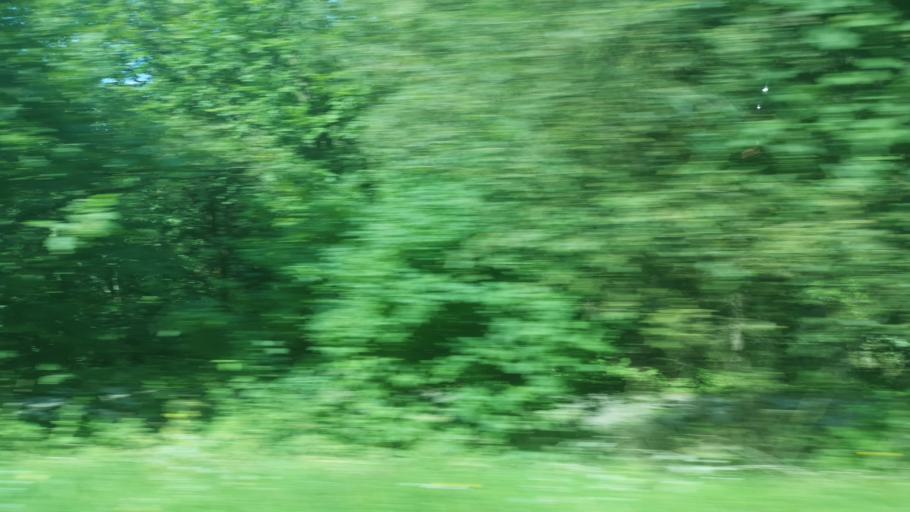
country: DE
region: Bavaria
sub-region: Upper Palatinate
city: Pemfling
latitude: 49.2829
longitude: 12.6254
